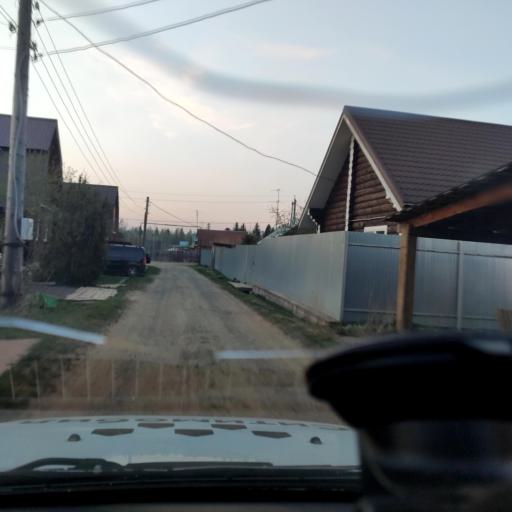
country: RU
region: Perm
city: Yug
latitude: 57.5873
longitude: 56.2000
